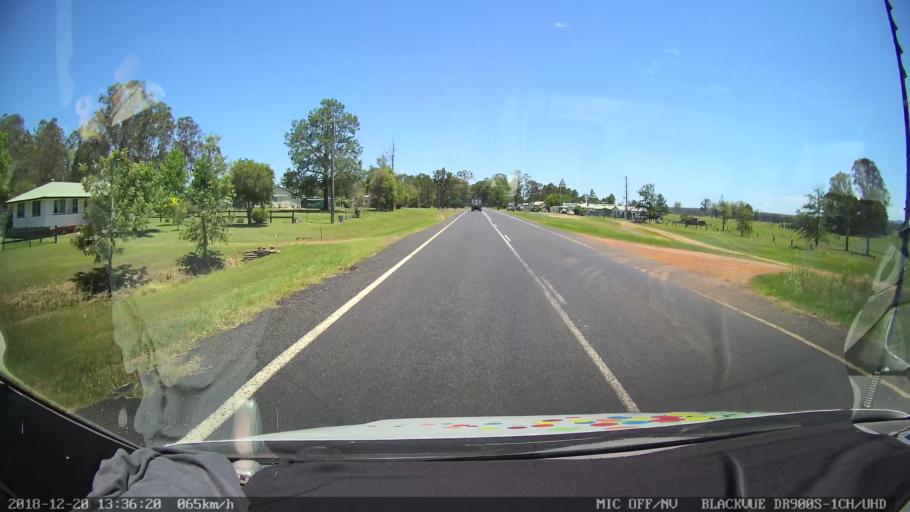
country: AU
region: New South Wales
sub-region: Clarence Valley
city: Maclean
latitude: -29.2807
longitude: 152.9901
